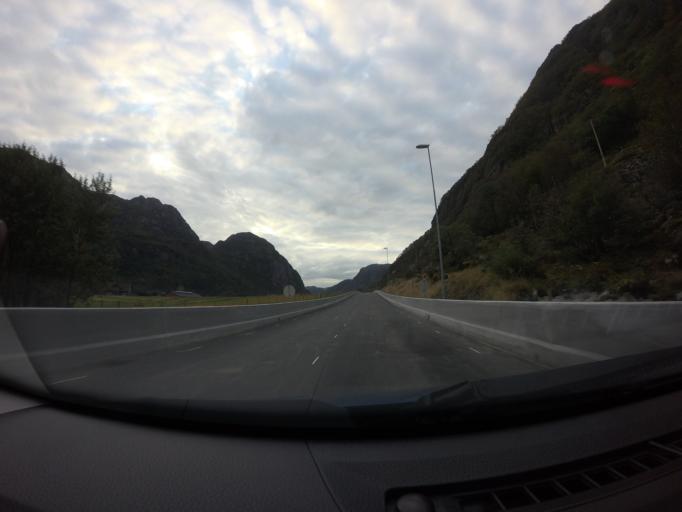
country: NO
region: Rogaland
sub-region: Forsand
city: Forsand
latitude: 58.8345
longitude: 6.1759
